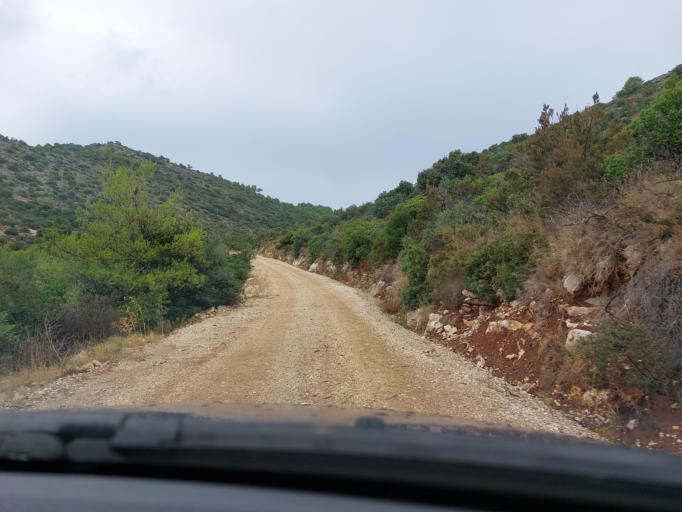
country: HR
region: Dubrovacko-Neretvanska
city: Smokvica
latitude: 42.7409
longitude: 16.9131
